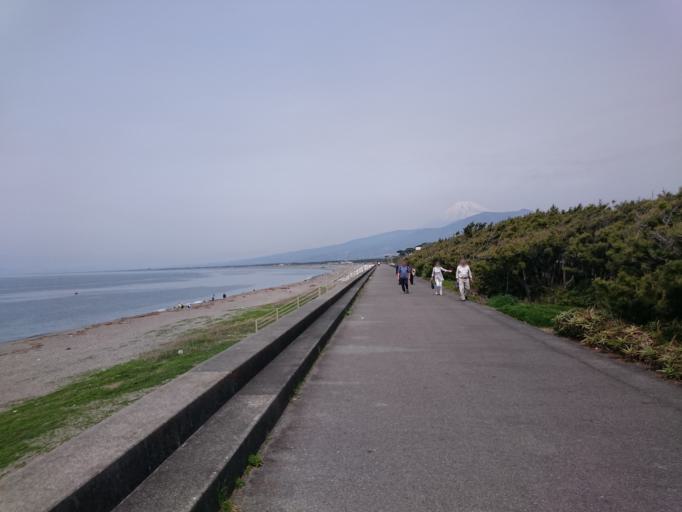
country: JP
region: Shizuoka
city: Numazu
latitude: 35.0882
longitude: 138.8505
